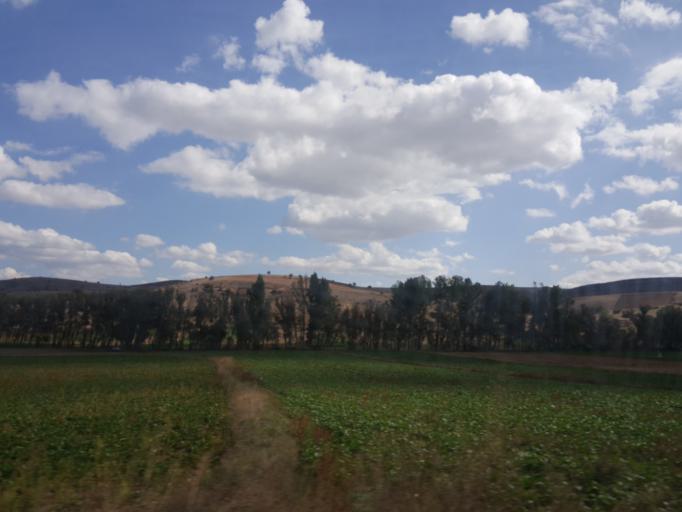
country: TR
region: Tokat
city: Camlibel
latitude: 40.1689
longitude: 36.4319
